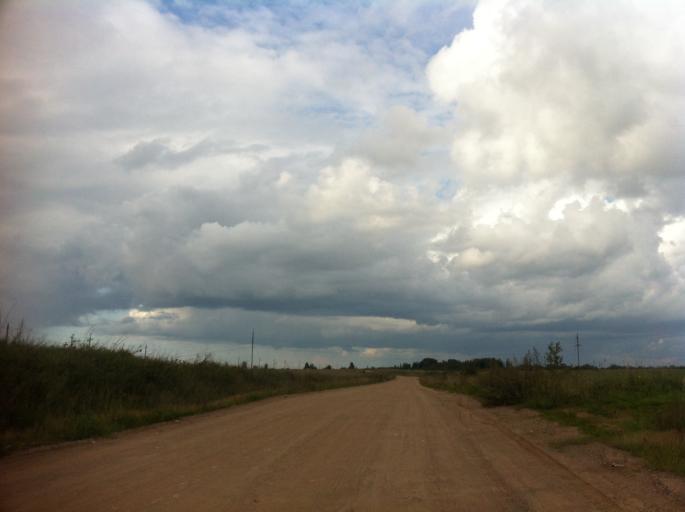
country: RU
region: Pskov
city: Izborsk
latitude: 57.8264
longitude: 27.9810
